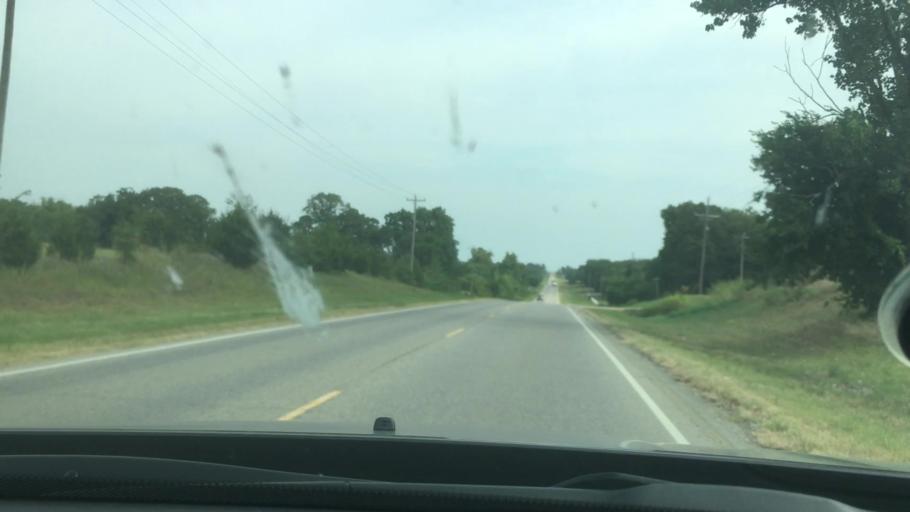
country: US
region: Oklahoma
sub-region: Johnston County
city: Tishomingo
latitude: 34.2523
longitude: -96.4248
